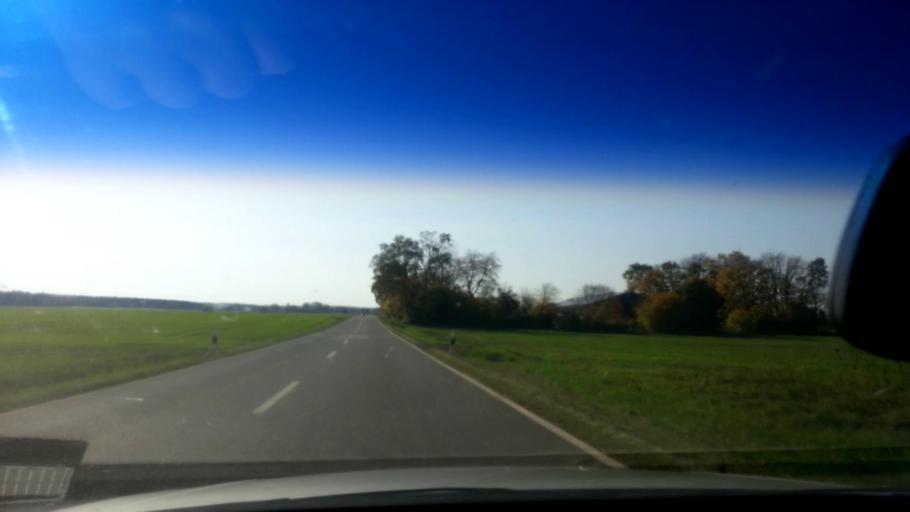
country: DE
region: Bavaria
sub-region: Upper Franconia
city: Wonsees
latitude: 49.9728
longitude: 11.2674
